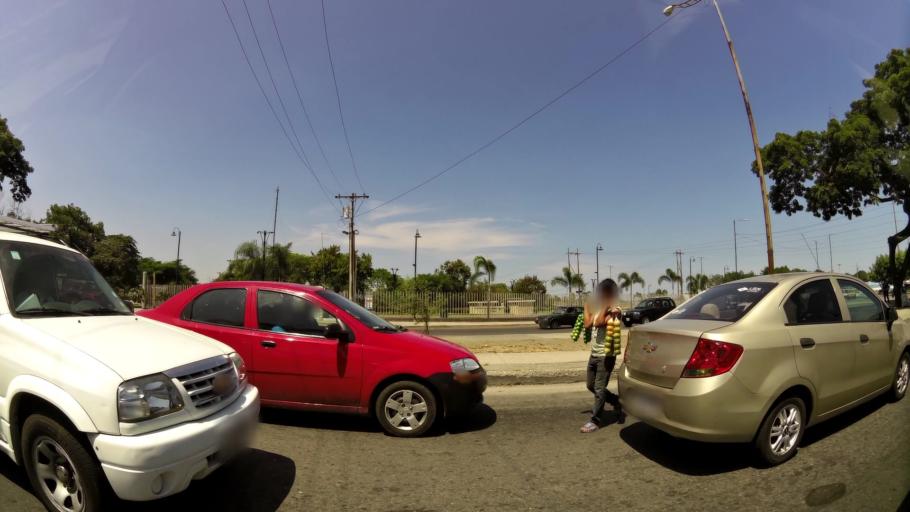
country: EC
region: Guayas
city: Guayaquil
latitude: -2.1939
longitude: -79.9372
